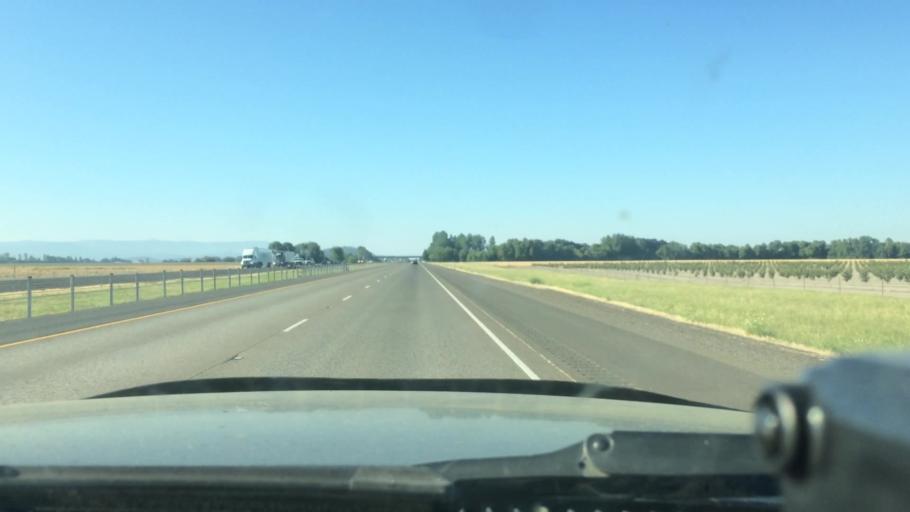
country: US
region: Oregon
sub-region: Linn County
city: Tangent
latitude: 44.5149
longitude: -123.0619
